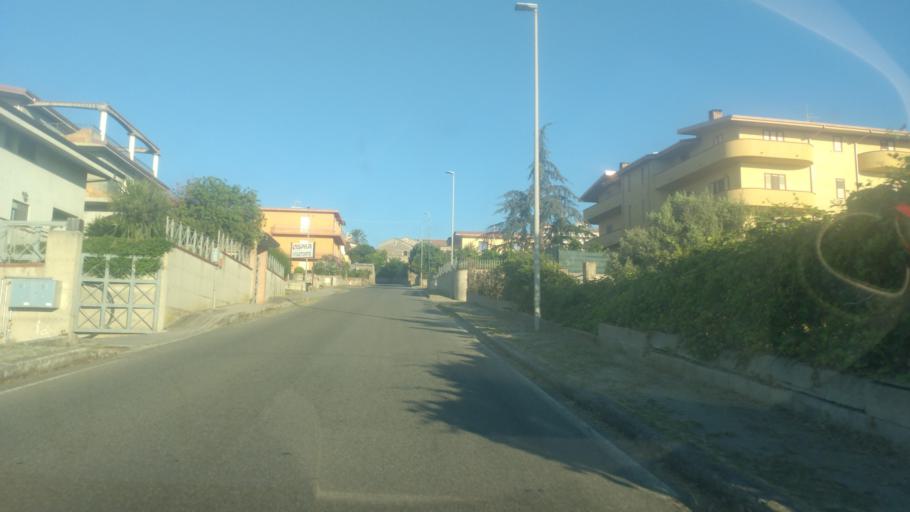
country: IT
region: Calabria
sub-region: Provincia di Catanzaro
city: Staletti
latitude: 38.7649
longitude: 16.5441
